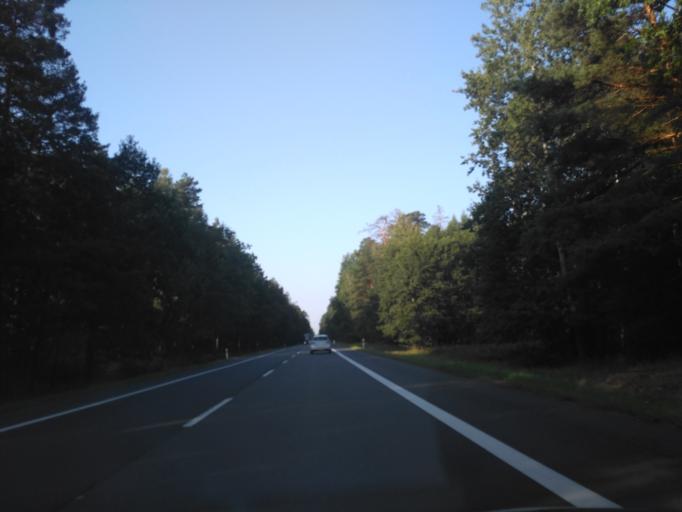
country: PL
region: Subcarpathian Voivodeship
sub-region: Powiat nizanski
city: Zarzecze
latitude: 50.5638
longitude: 22.2474
